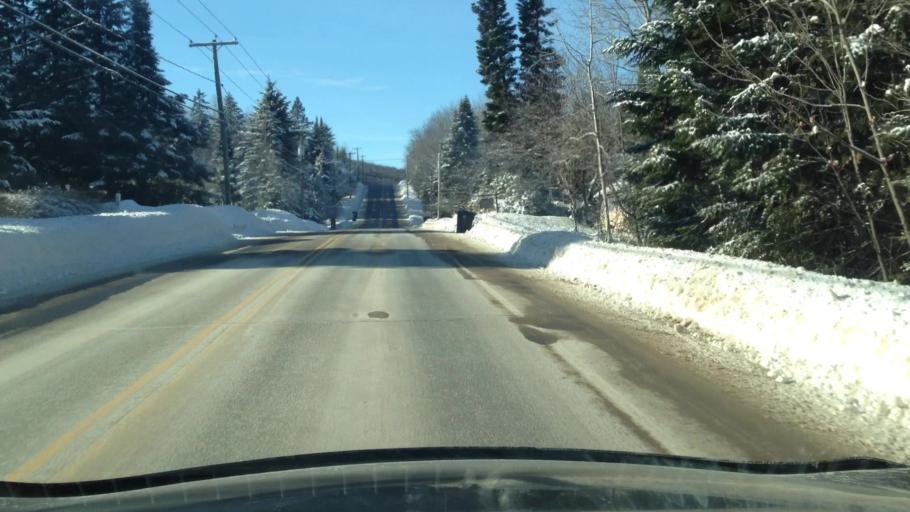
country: CA
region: Quebec
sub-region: Laurentides
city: Sainte-Agathe-des-Monts
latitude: 45.9309
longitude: -74.4223
